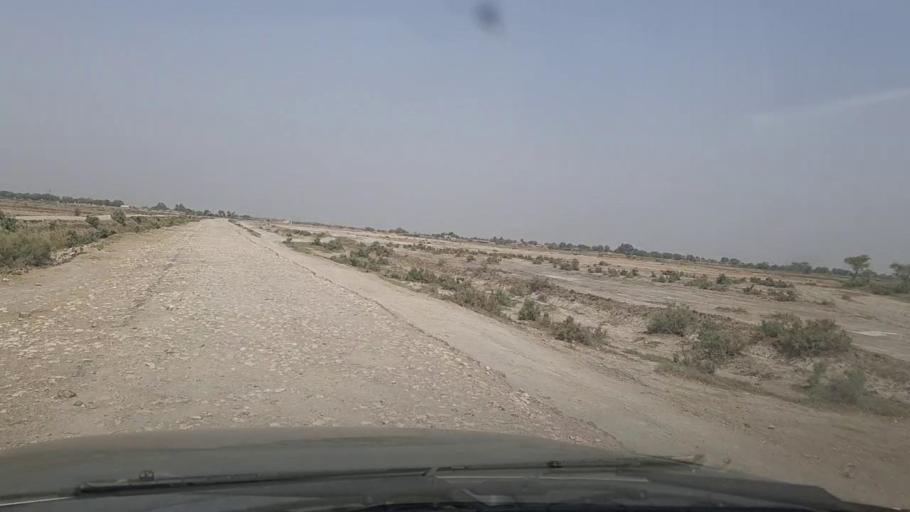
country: PK
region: Balochistan
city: Sohbatpur
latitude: 28.4120
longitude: 68.6953
